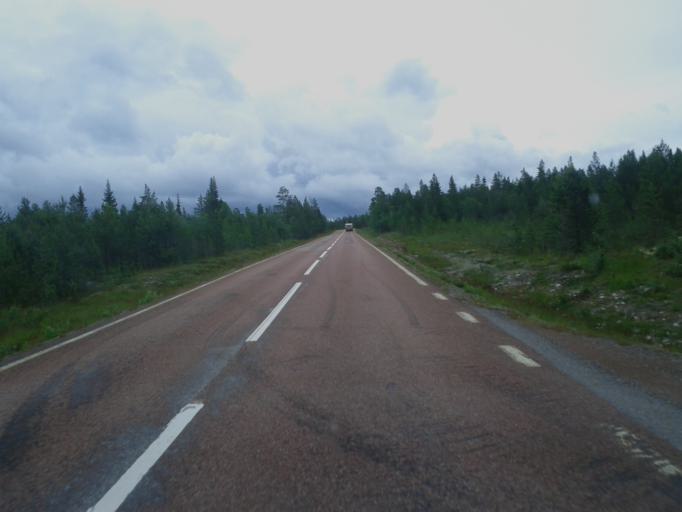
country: NO
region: Hedmark
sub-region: Engerdal
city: Engerdal
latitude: 61.8036
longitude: 12.3759
